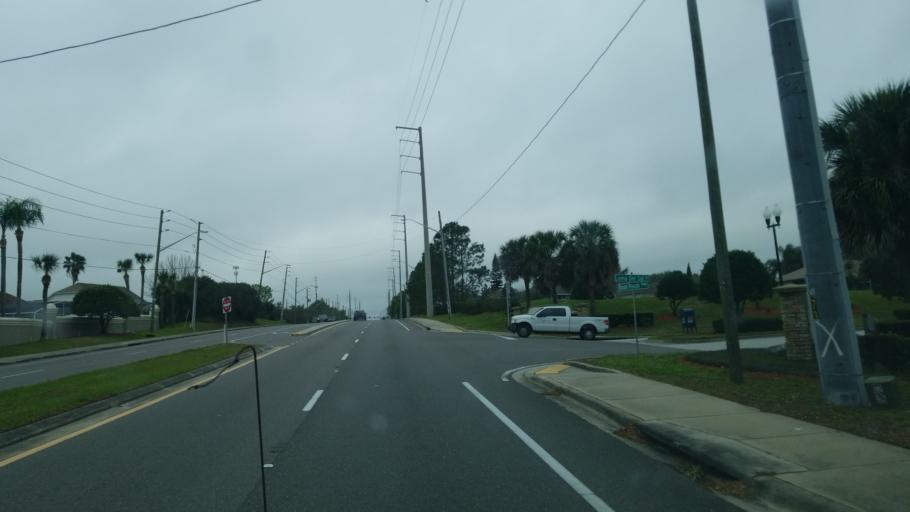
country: US
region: Florida
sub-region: Lake County
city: Four Corners
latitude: 28.2566
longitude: -81.6458
